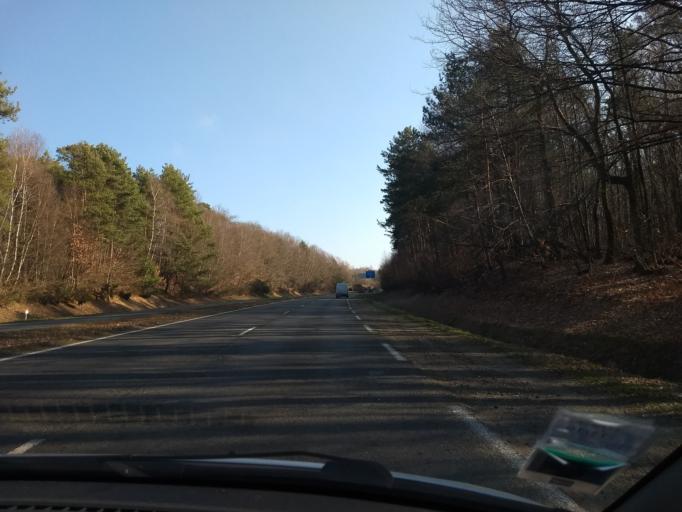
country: FR
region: Limousin
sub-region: Departement de la Haute-Vienne
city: Le Palais-sur-Vienne
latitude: 45.8713
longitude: 1.2822
